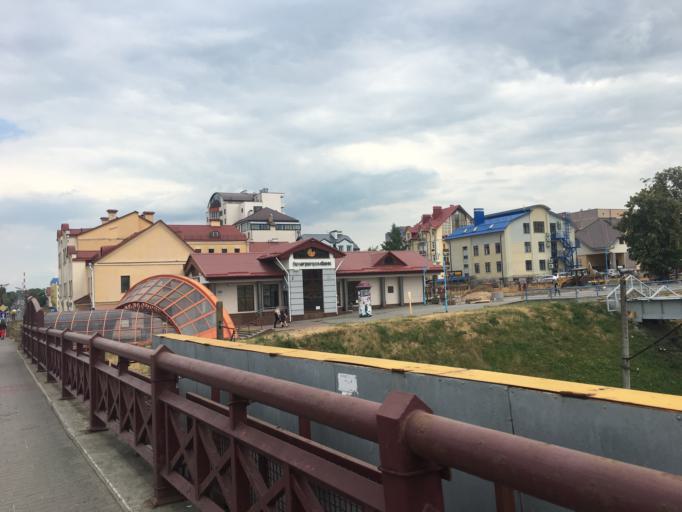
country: BY
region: Grodnenskaya
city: Hrodna
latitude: 53.6766
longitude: 23.8404
